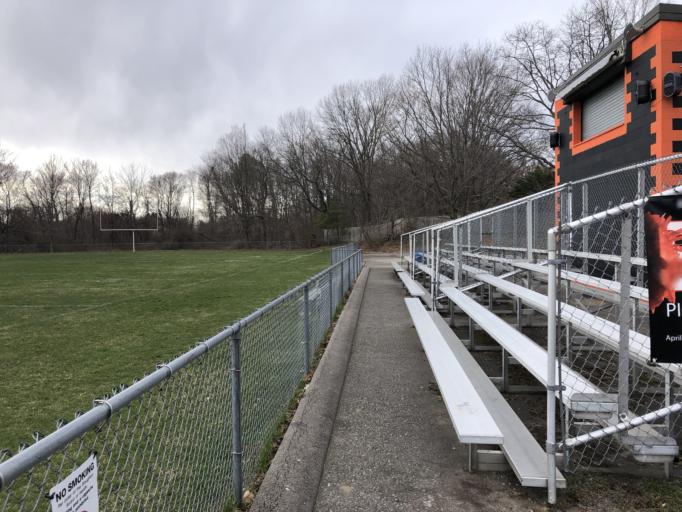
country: US
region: Massachusetts
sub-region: Norfolk County
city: Stoughton
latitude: 42.1295
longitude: -71.1035
